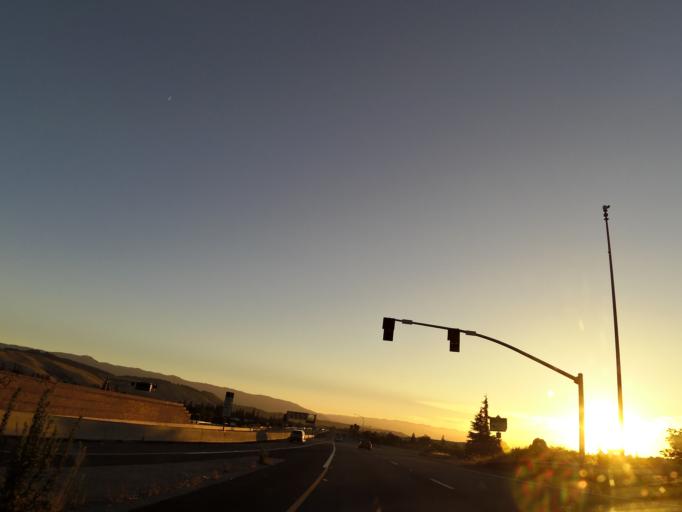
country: US
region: California
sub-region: Santa Clara County
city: Seven Trees
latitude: 37.2420
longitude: -121.7710
